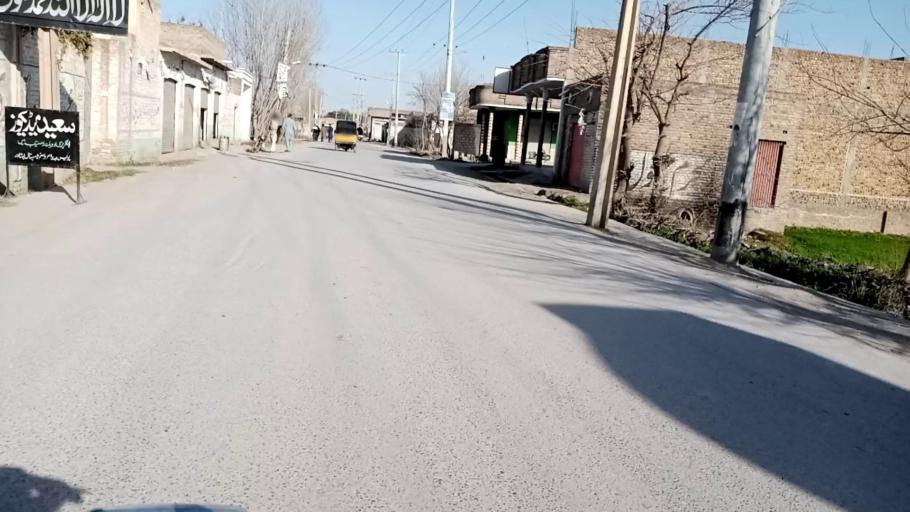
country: PK
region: Khyber Pakhtunkhwa
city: Peshawar
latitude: 34.0551
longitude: 71.5351
